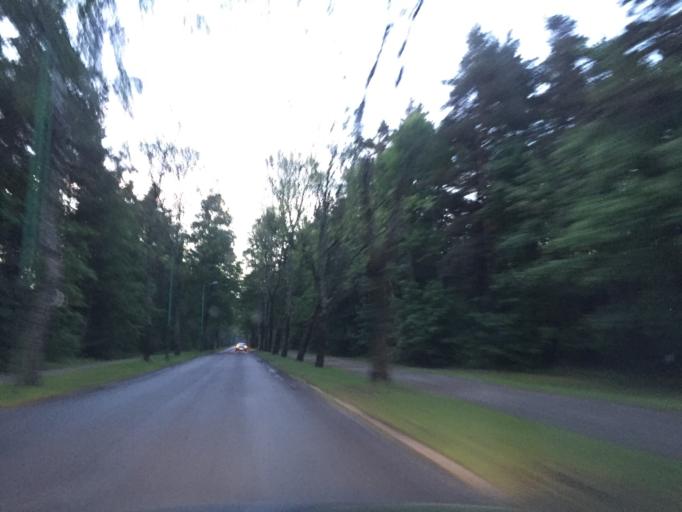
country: LT
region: Klaipedos apskritis
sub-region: Klaipeda
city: Palanga
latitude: 55.8969
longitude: 21.0615
